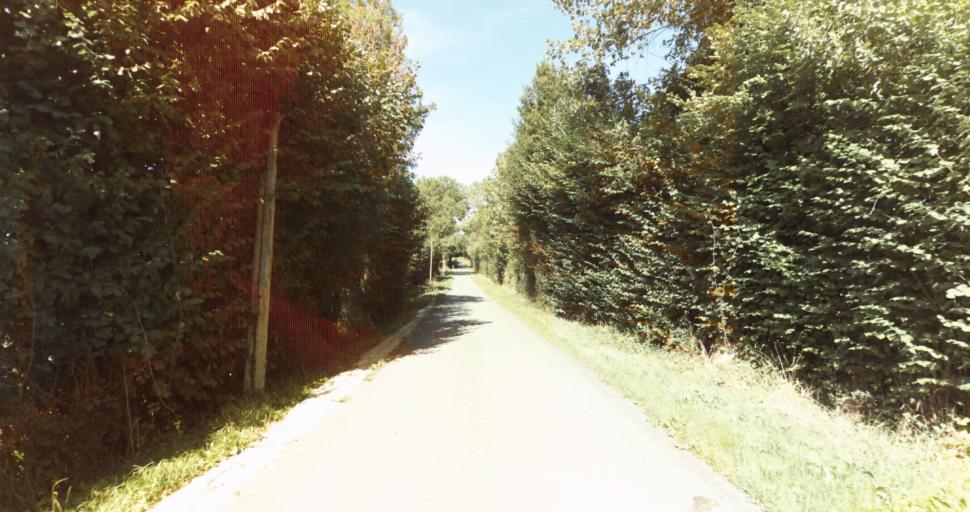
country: FR
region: Lower Normandy
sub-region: Departement de l'Orne
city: Gace
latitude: 48.7352
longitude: 0.2387
